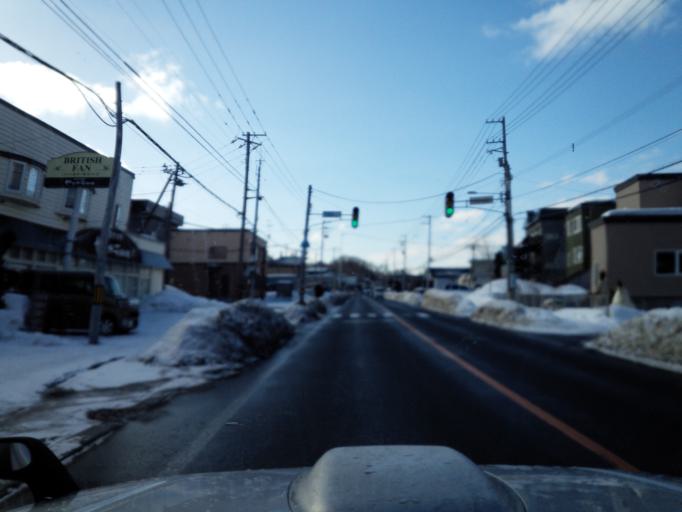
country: JP
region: Hokkaido
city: Sapporo
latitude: 42.9489
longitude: 141.3469
